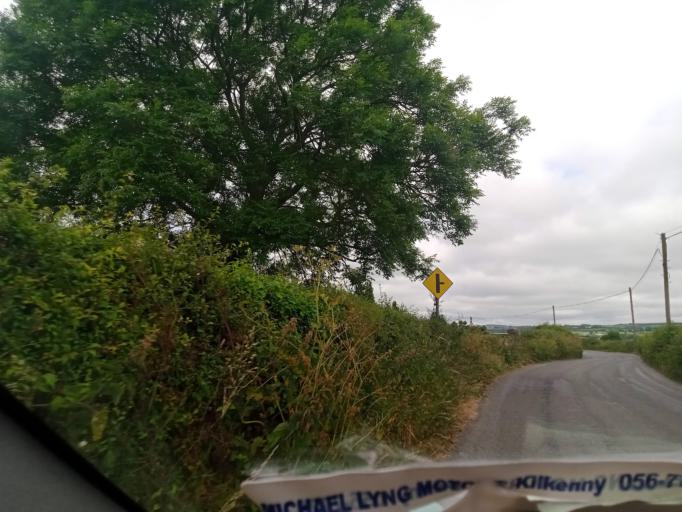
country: IE
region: Leinster
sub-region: Kilkenny
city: Ballyragget
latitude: 52.7522
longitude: -7.4412
